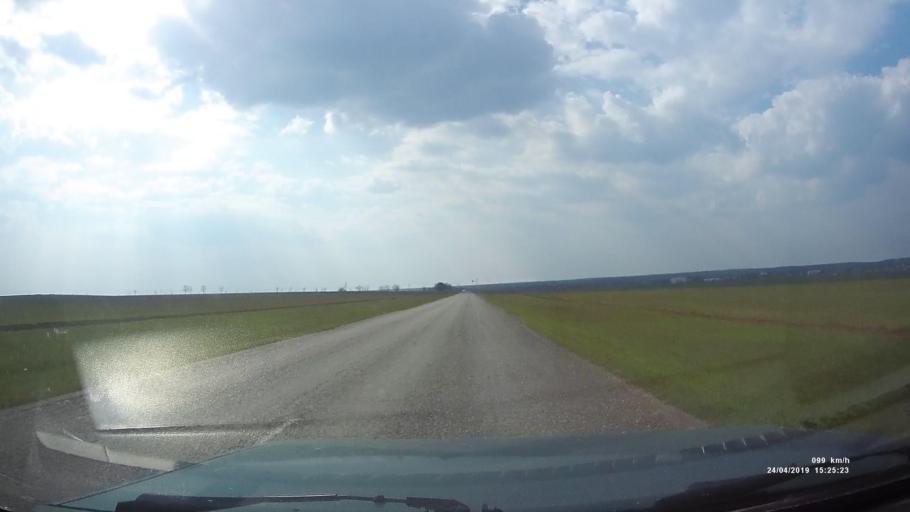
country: RU
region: Rostov
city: Remontnoye
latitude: 46.5522
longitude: 43.0490
